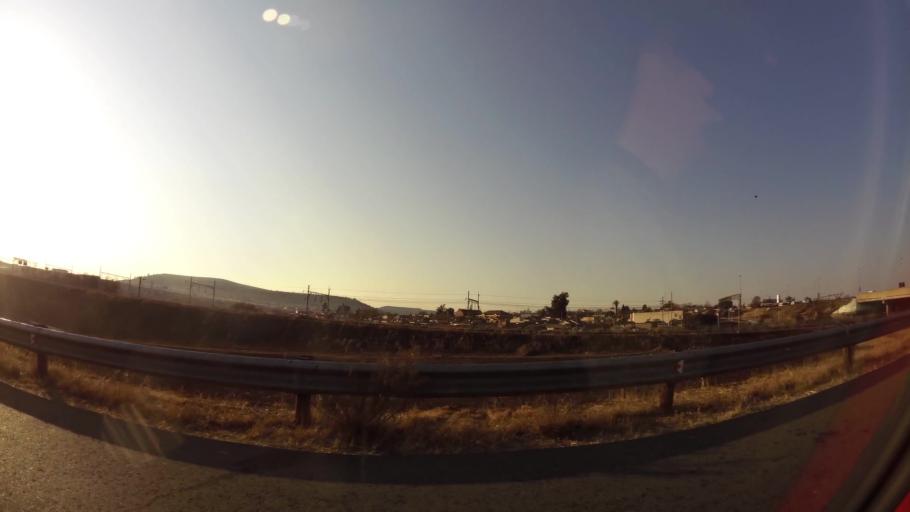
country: ZA
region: Gauteng
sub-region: City of Johannesburg Metropolitan Municipality
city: Soweto
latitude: -26.2237
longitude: 27.9298
